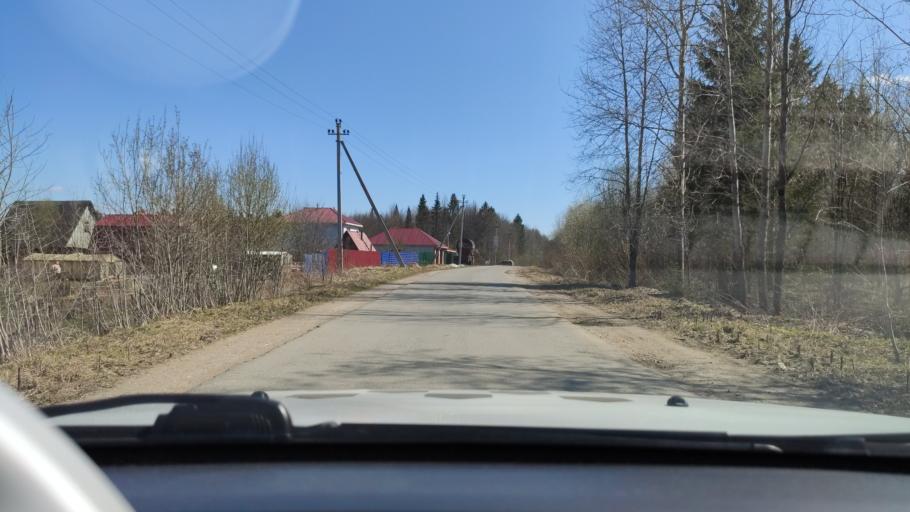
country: RU
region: Perm
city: Novyye Lyady
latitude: 58.0440
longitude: 56.6172
